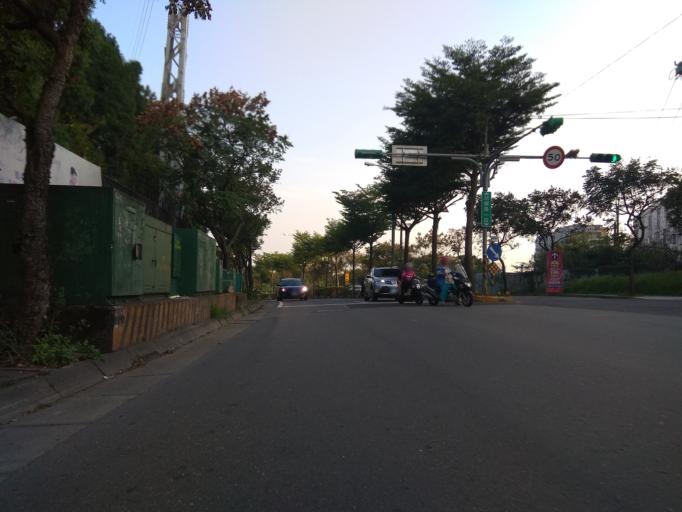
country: TW
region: Taiwan
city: Daxi
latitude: 24.9230
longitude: 121.1778
